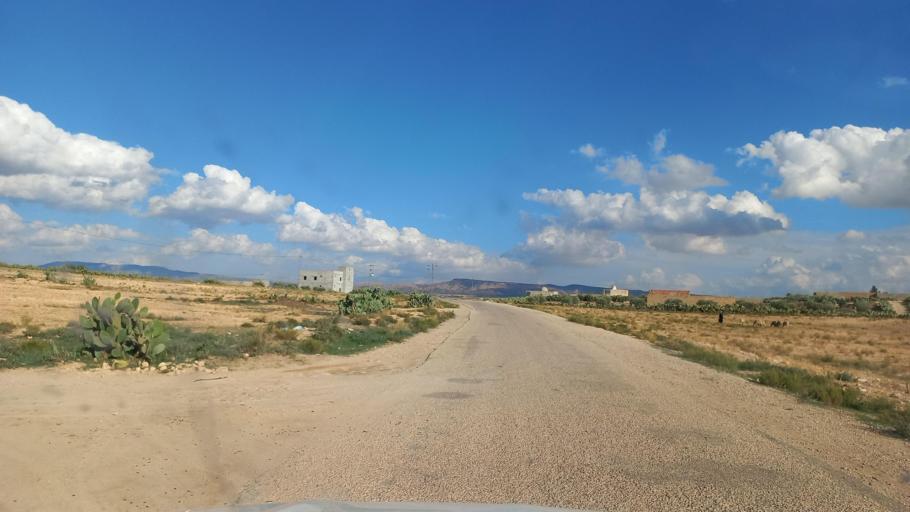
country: TN
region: Al Qasrayn
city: Sbiba
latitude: 35.3835
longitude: 9.0414
